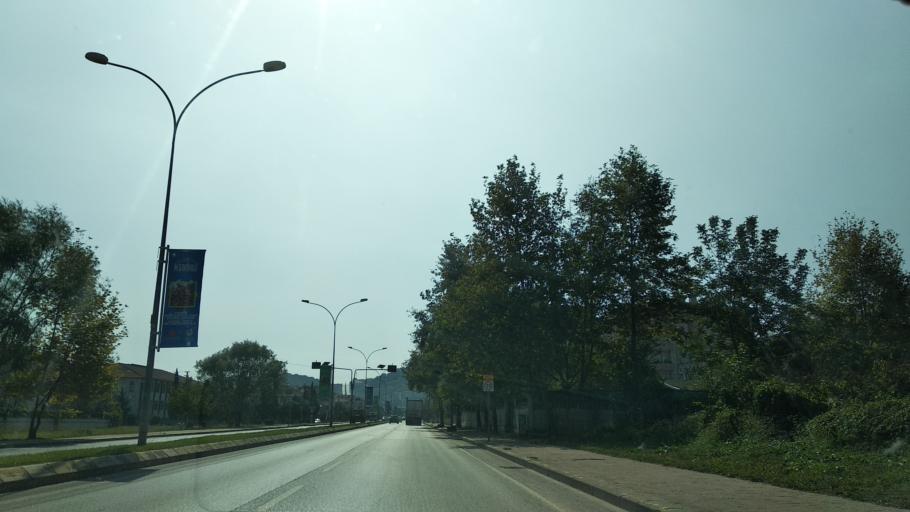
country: TR
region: Sakarya
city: Adapazari
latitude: 40.7677
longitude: 30.3638
